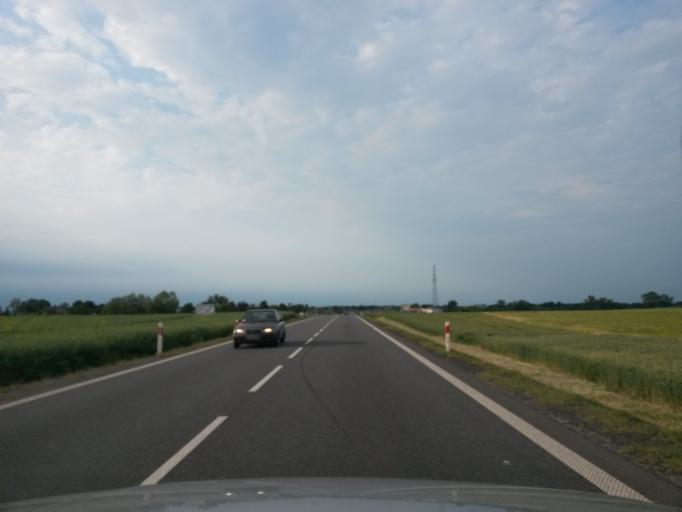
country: PL
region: Lower Silesian Voivodeship
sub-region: Powiat sredzki
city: Ciechow
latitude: 51.0314
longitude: 16.5809
